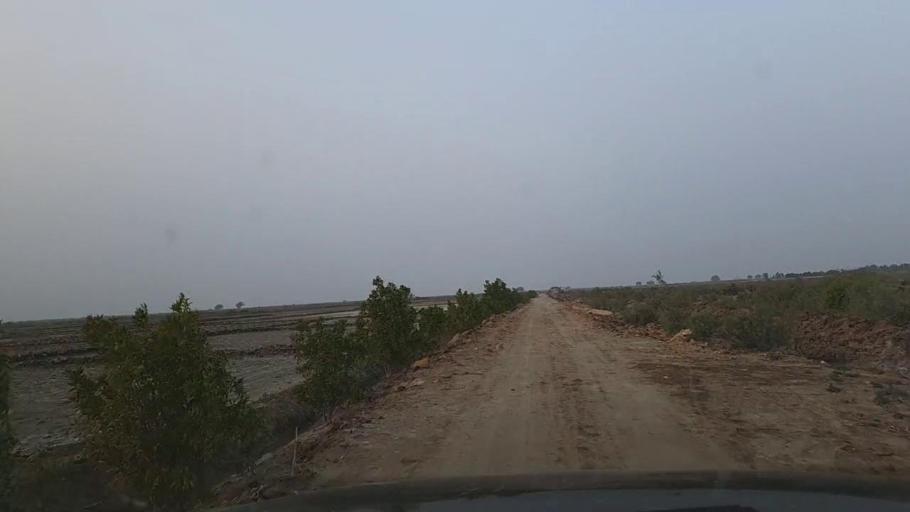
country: PK
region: Sindh
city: Gharo
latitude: 24.7431
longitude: 67.7204
